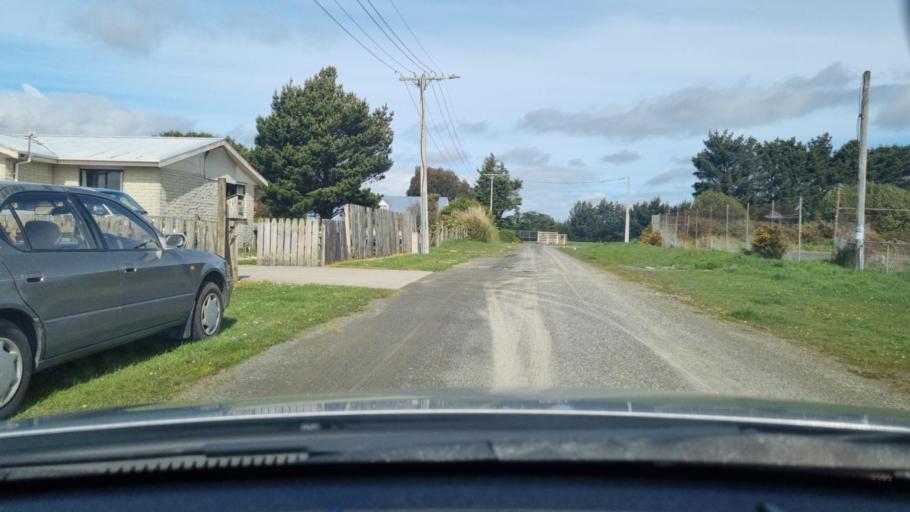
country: NZ
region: Southland
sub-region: Invercargill City
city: Invercargill
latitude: -46.4542
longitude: 168.3708
